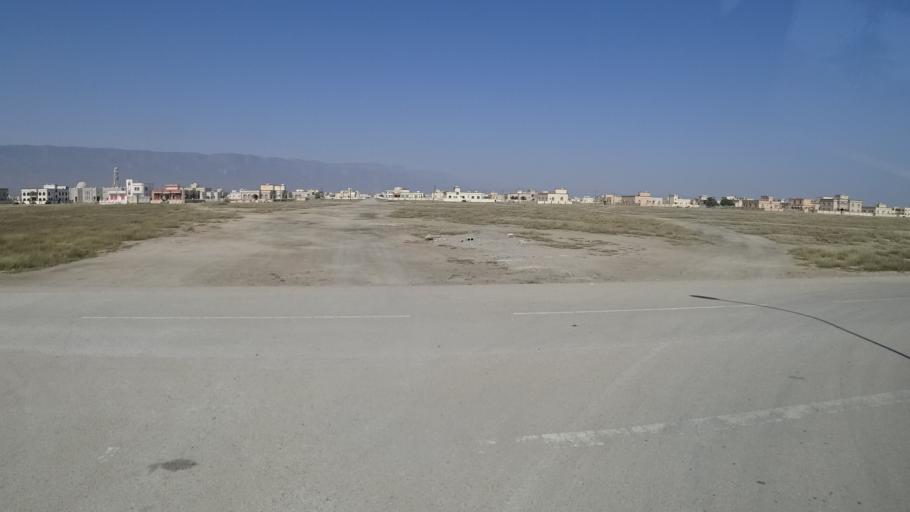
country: OM
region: Zufar
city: Salalah
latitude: 16.9859
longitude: 54.7088
